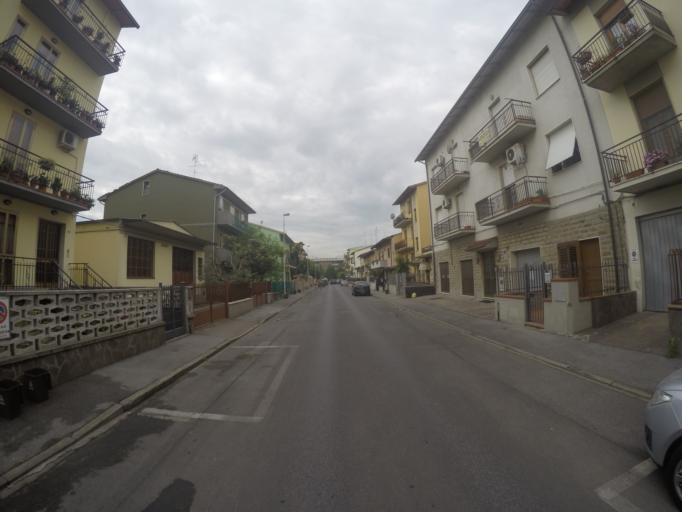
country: IT
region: Tuscany
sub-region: Provincia di Prato
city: Prato
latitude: 43.8991
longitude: 11.0672
